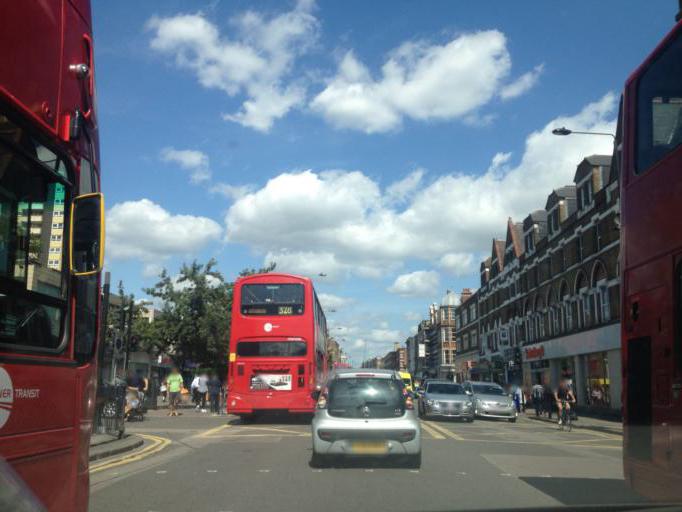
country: GB
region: England
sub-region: Greater London
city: Belsize Park
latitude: 51.5383
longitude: -0.1939
